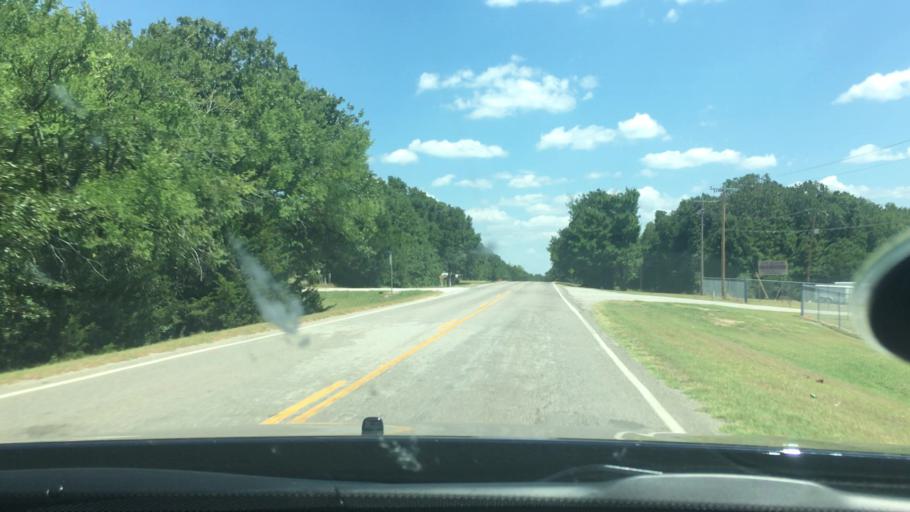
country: US
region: Oklahoma
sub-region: Carter County
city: Dickson
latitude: 34.1957
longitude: -96.9840
